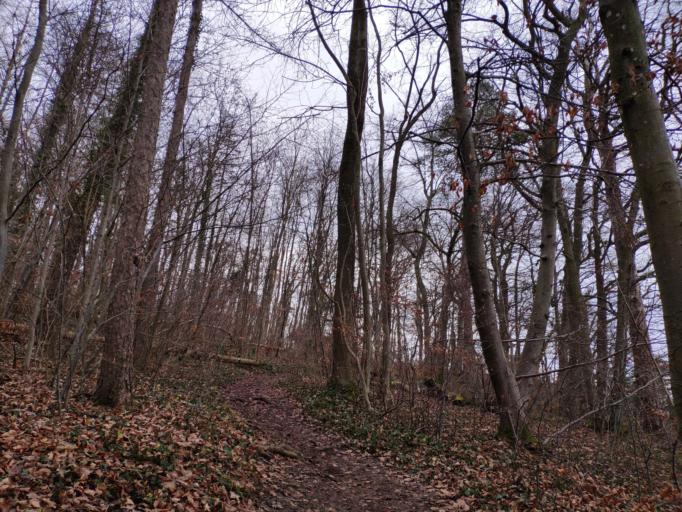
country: CH
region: Basel-City
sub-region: Basel-Stadt
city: Riehen
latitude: 47.5595
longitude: 7.6462
